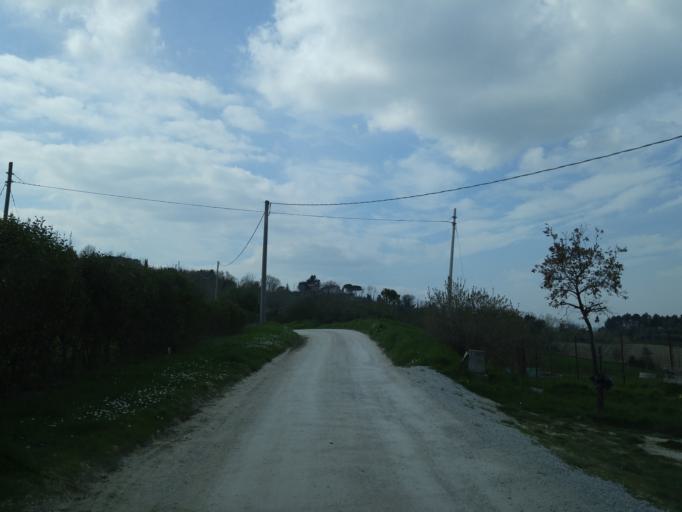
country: IT
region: The Marches
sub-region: Provincia di Pesaro e Urbino
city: Villanova
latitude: 43.7251
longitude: 12.9354
